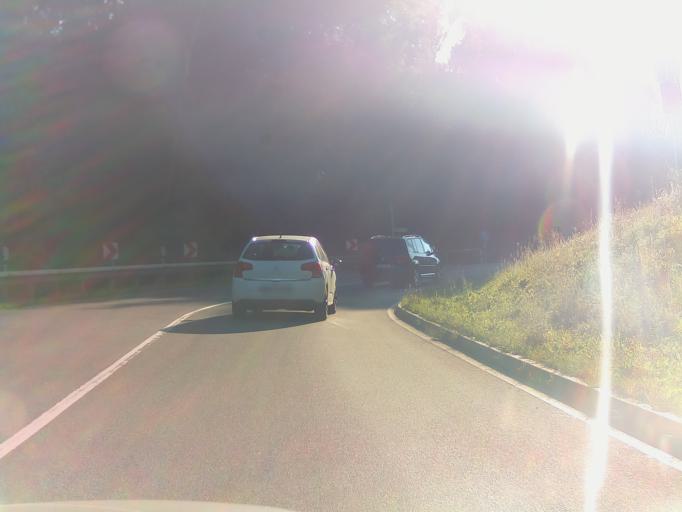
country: DE
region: Bavaria
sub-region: Regierungsbezirk Unterfranken
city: Gaukonigshofen
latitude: 49.6519
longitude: 10.0280
